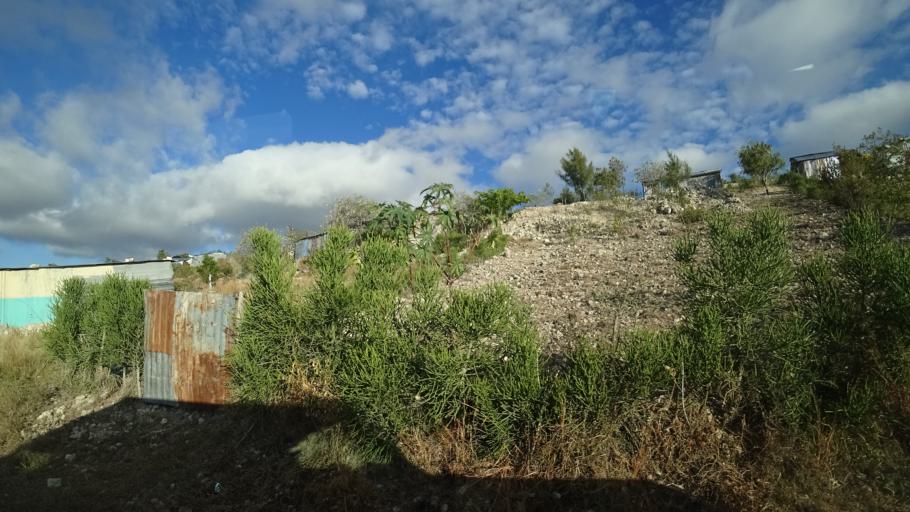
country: HT
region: Ouest
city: Croix des Bouquets
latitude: 18.6721
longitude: -72.2613
